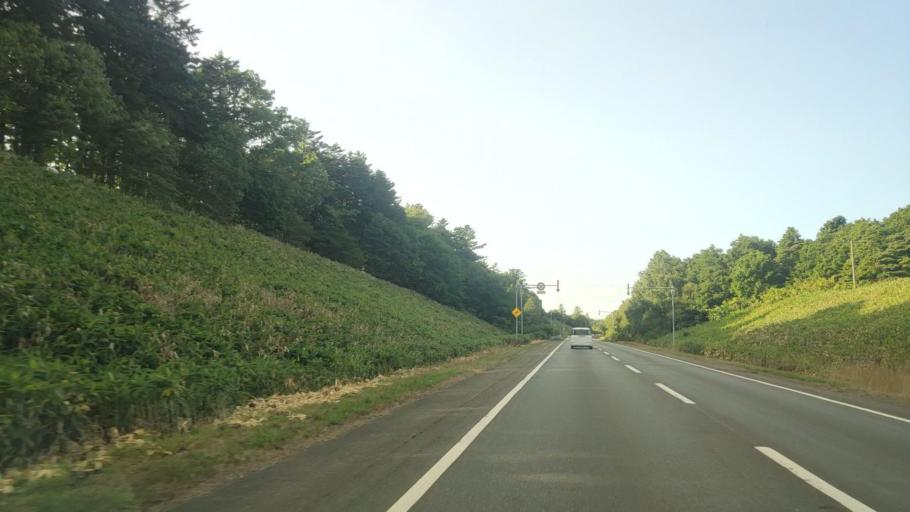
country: JP
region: Hokkaido
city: Makubetsu
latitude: 45.0644
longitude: 141.7482
